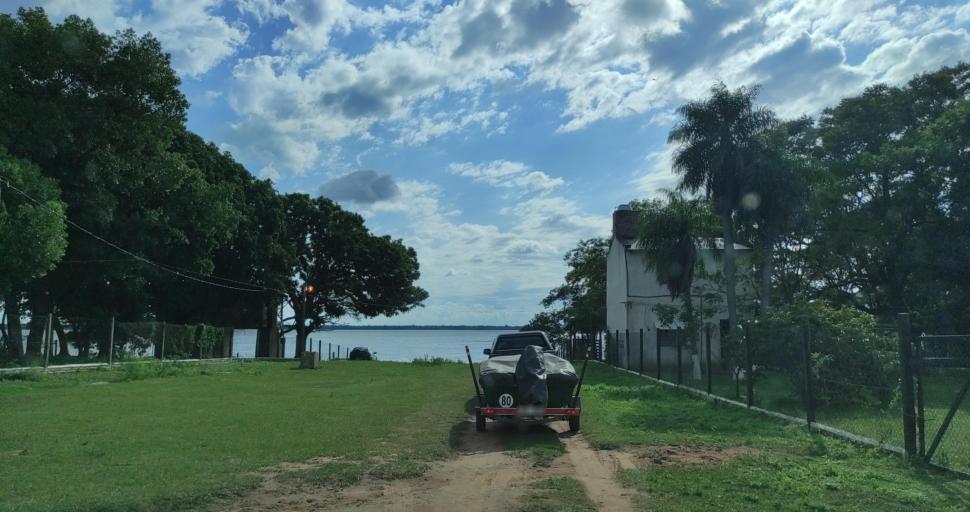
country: AR
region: Corrientes
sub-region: Departamento de Itati
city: Itati
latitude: -27.2671
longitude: -58.2520
